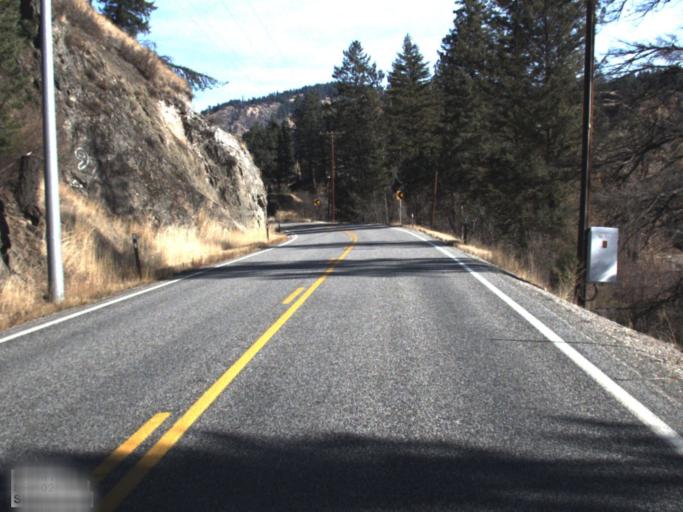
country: CA
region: British Columbia
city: Grand Forks
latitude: 48.9074
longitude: -118.5710
